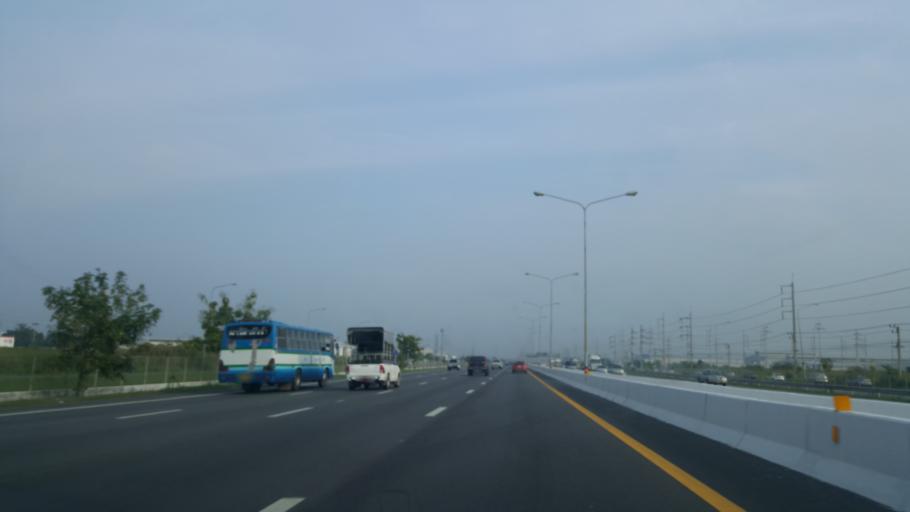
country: TH
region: Chon Buri
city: Phan Thong
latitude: 13.4304
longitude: 101.0465
